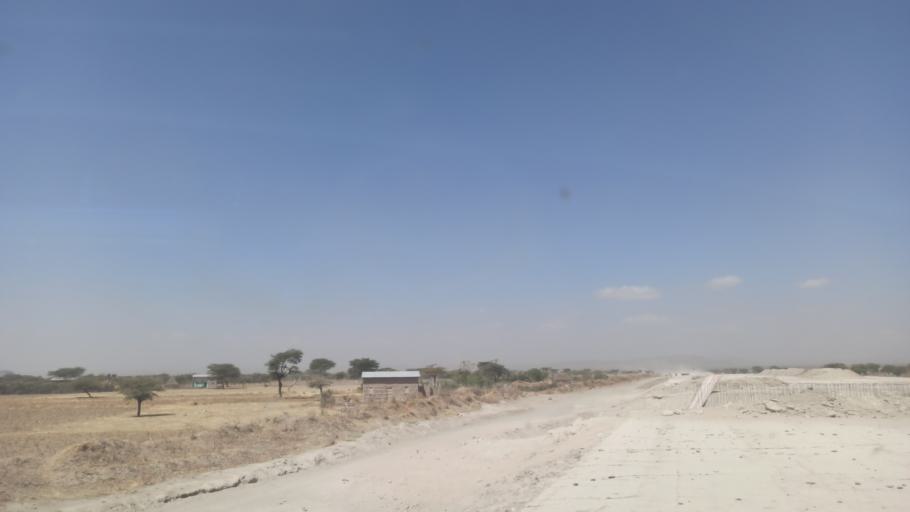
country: ET
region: Oromiya
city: Ziway
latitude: 7.7209
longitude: 38.6306
